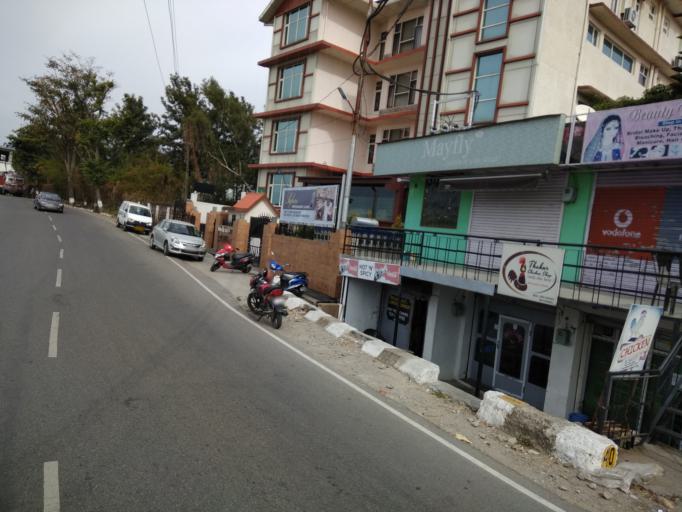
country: IN
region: Himachal Pradesh
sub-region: Kangra
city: Dharmsala
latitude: 32.1931
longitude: 76.3478
